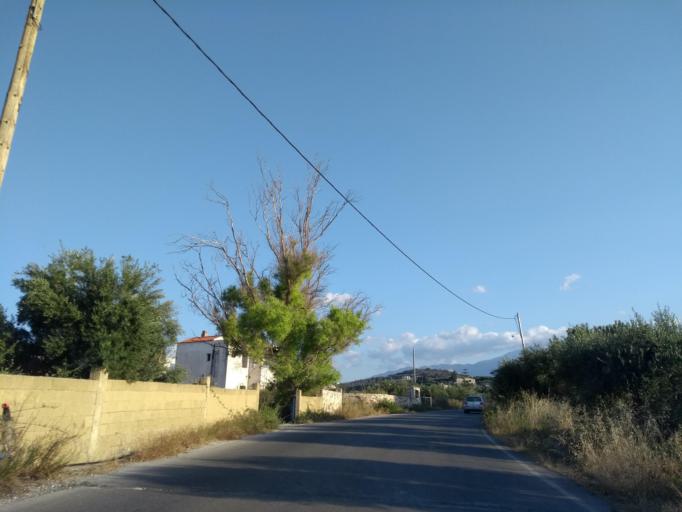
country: GR
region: Crete
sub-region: Nomos Chanias
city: Kalivai
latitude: 35.4437
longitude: 24.1761
